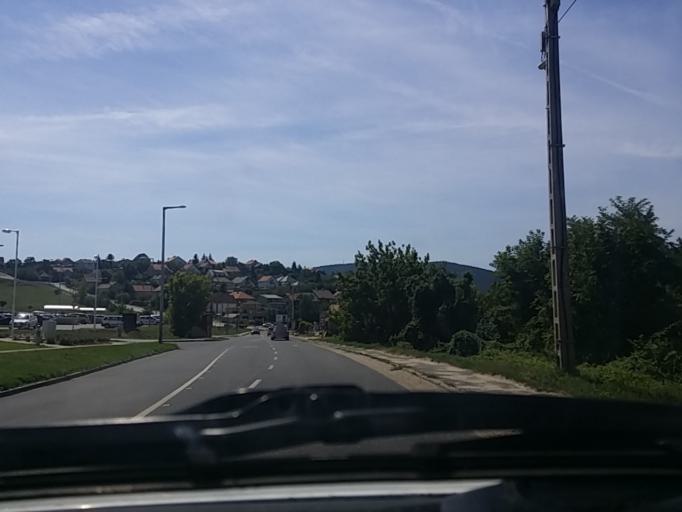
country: HU
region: Pest
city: Urom
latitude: 47.5913
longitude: 19.0102
